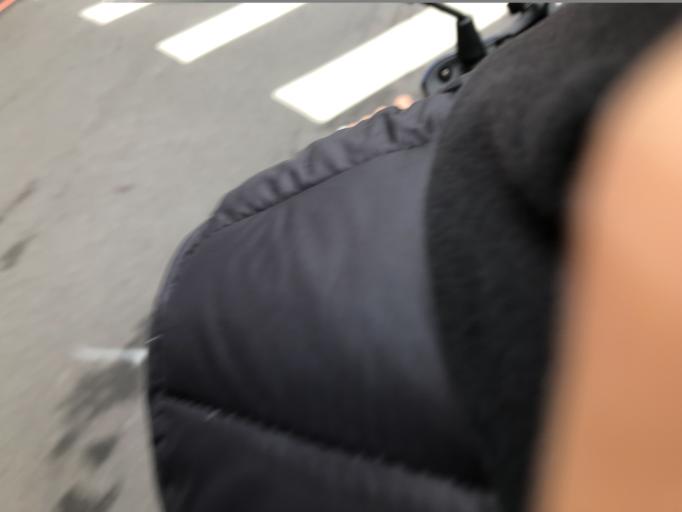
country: TW
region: Taiwan
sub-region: Taoyuan
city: Taoyuan
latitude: 25.0636
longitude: 121.3610
